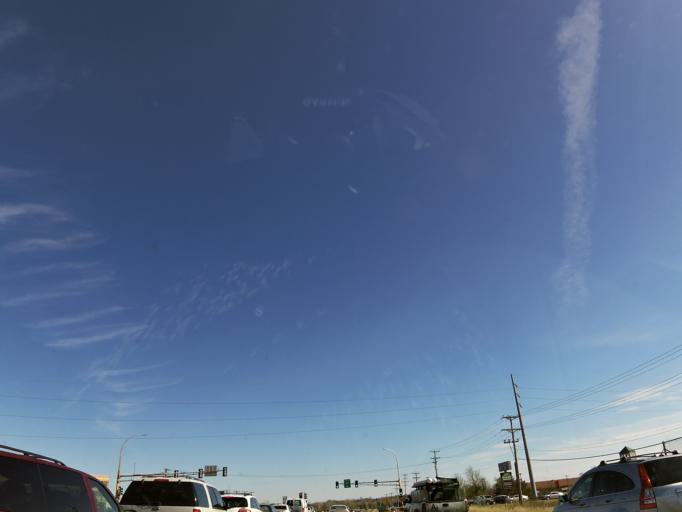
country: US
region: Minnesota
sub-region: Hennepin County
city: Plymouth
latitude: 45.0107
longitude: -93.4570
